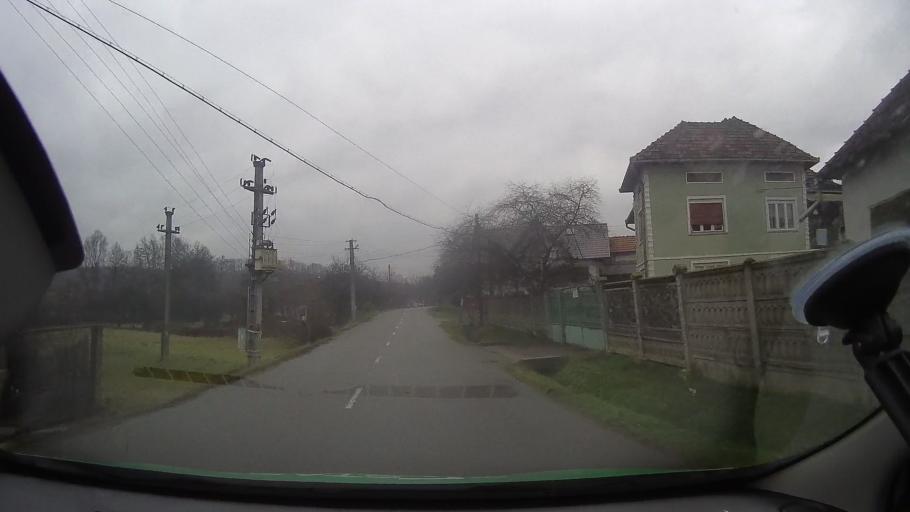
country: RO
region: Hunedoara
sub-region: Comuna Tomesti
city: Tomesti
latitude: 46.2116
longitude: 22.6654
